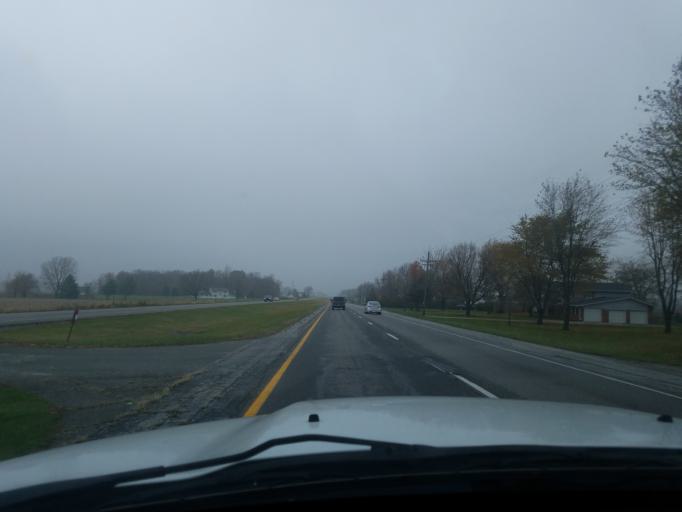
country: US
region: Indiana
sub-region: Howard County
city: Indian Heights
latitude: 40.3502
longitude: -86.1271
